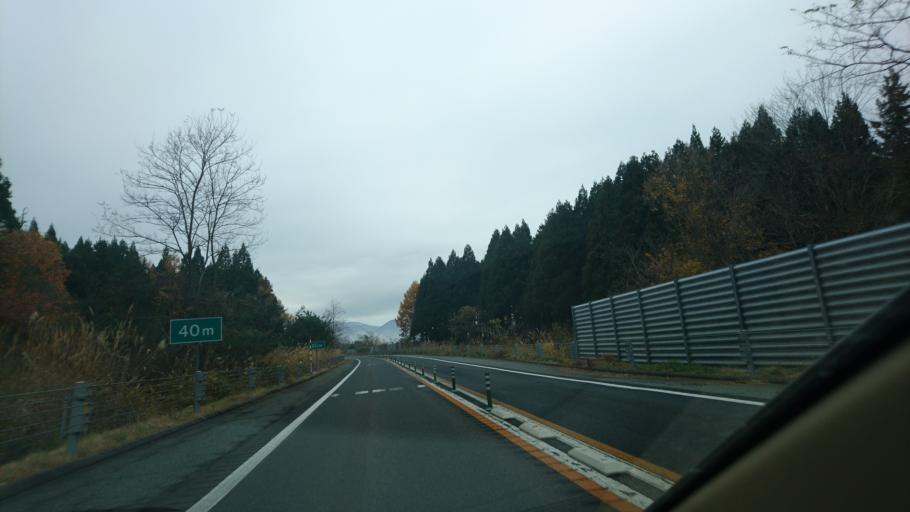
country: JP
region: Iwate
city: Kitakami
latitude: 39.2809
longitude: 141.0285
